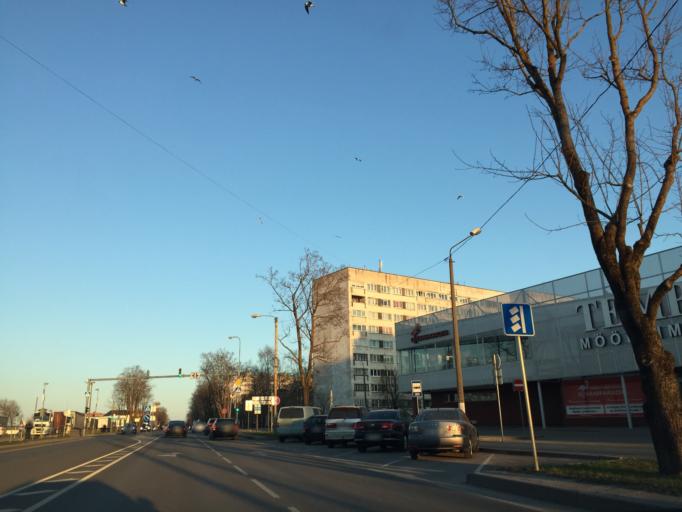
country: EE
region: Ida-Virumaa
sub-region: Narva linn
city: Narva
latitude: 59.3829
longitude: 28.1649
